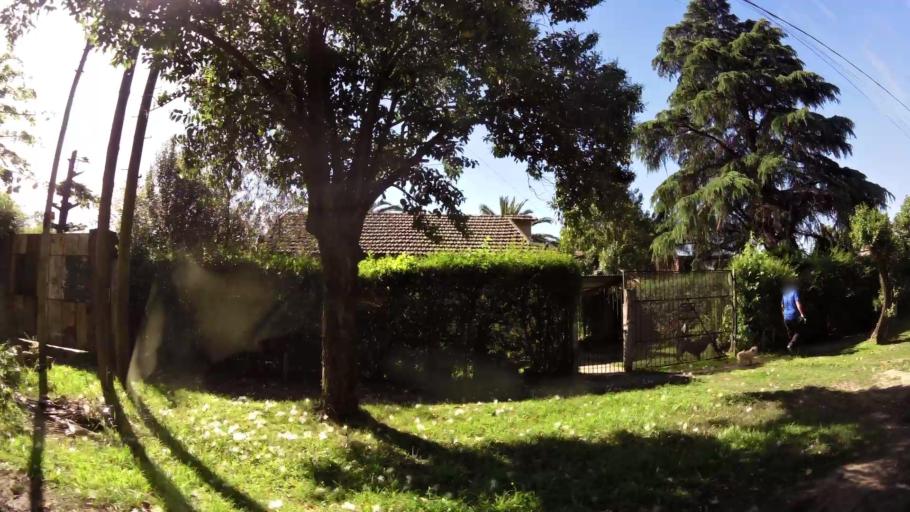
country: AR
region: Buenos Aires
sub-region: Partido de Almirante Brown
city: Adrogue
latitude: -34.7991
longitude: -58.3532
